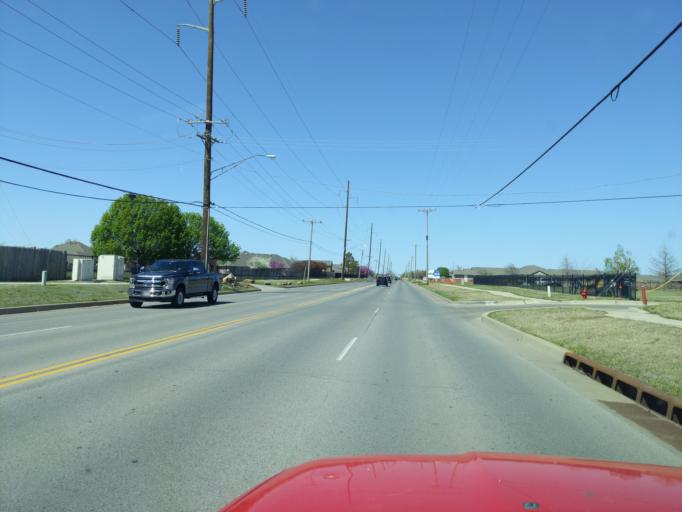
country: US
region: Oklahoma
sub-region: Cleveland County
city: Moore
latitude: 35.3268
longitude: -97.5120
